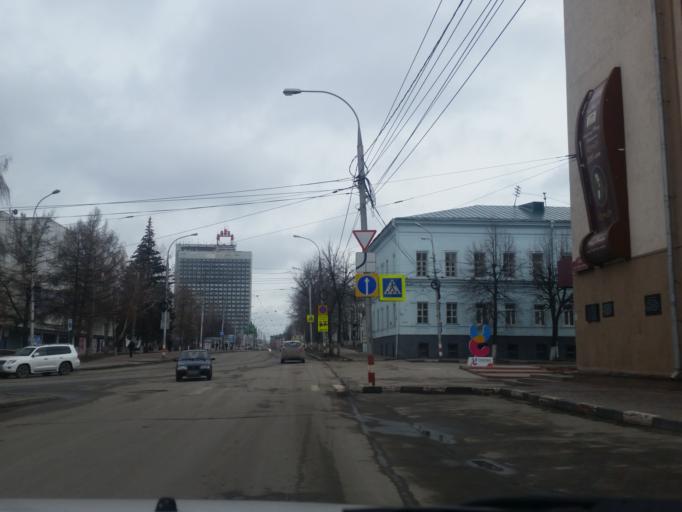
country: RU
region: Ulyanovsk
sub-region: Ulyanovskiy Rayon
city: Ulyanovsk
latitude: 54.3150
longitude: 48.4010
